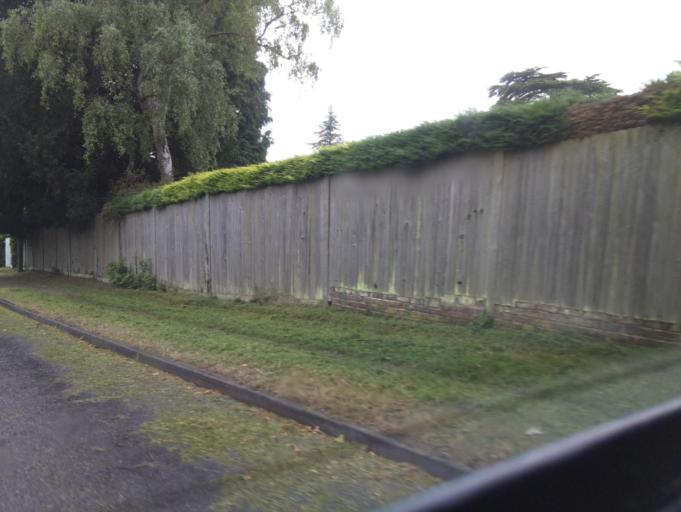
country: GB
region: England
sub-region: Surrey
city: Reigate
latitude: 51.2486
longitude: -0.1959
